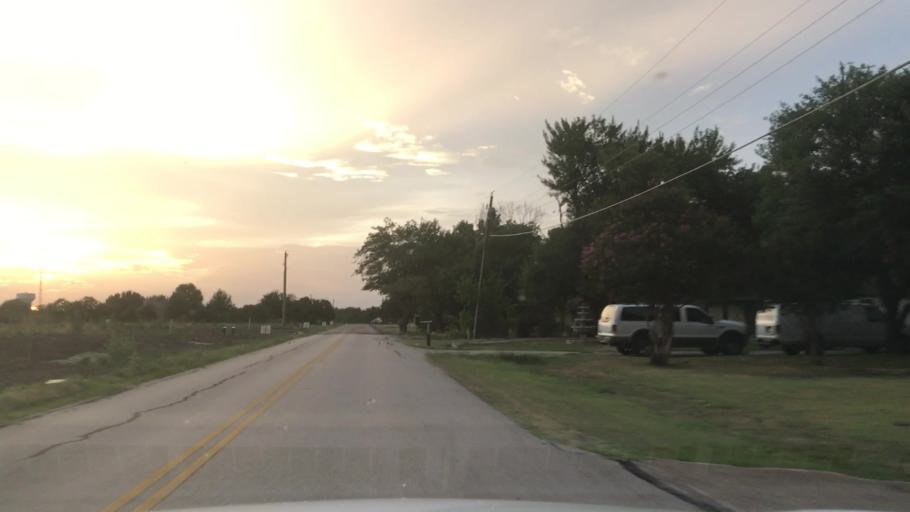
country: US
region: Texas
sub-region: Dallas County
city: Seagoville
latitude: 32.6997
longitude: -96.5522
